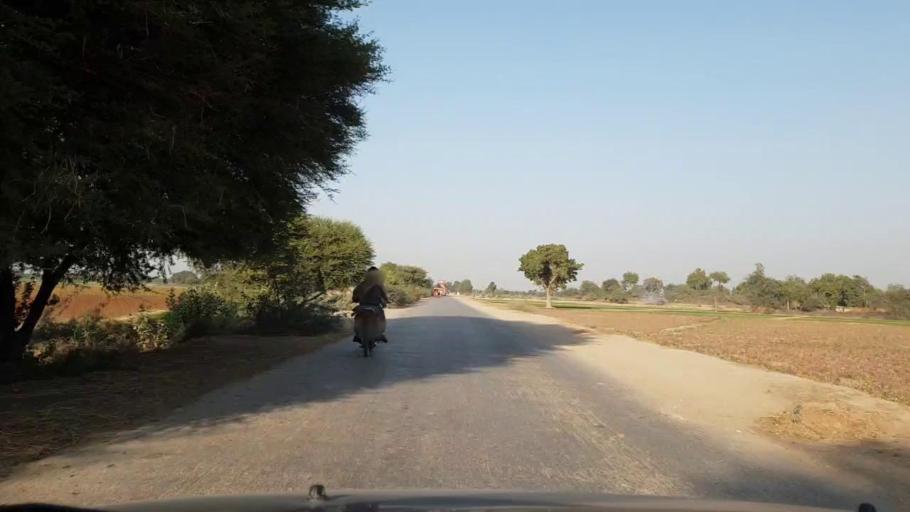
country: PK
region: Sindh
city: Chambar
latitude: 25.2215
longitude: 68.7817
